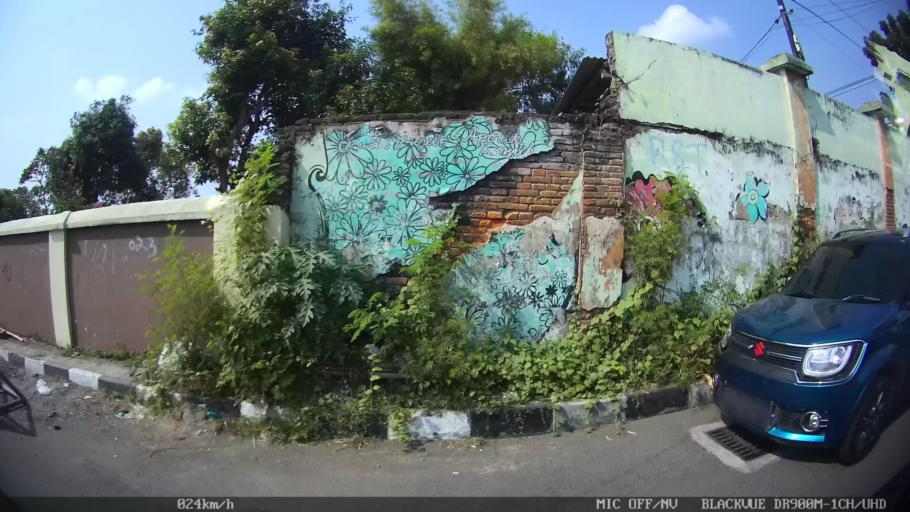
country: ID
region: Daerah Istimewa Yogyakarta
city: Yogyakarta
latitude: -7.8081
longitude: 110.3716
